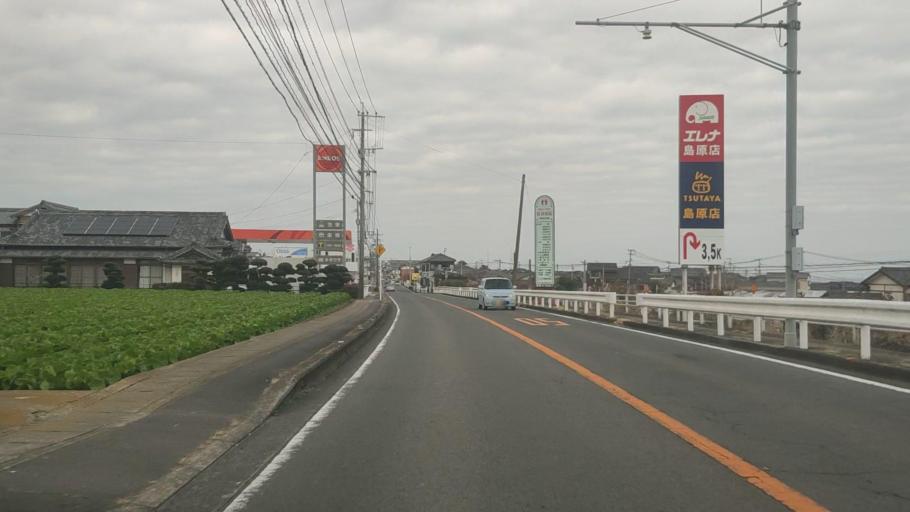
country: JP
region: Nagasaki
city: Shimabara
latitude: 32.8220
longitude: 130.3535
